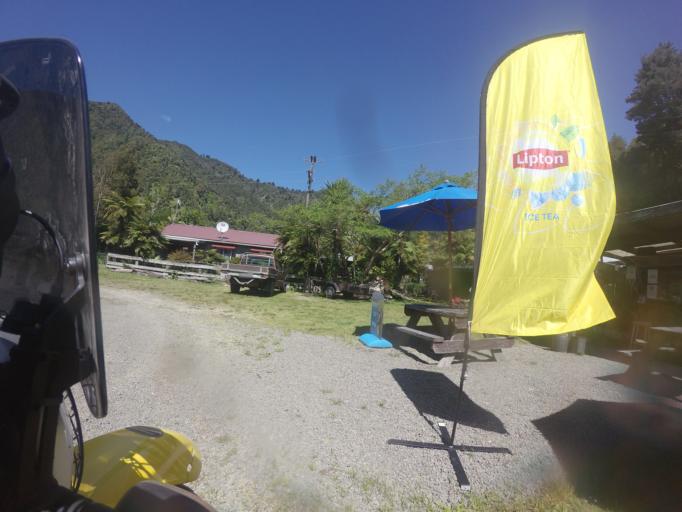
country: NZ
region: Bay of Plenty
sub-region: Opotiki District
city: Opotiki
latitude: -38.2779
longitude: 177.3443
